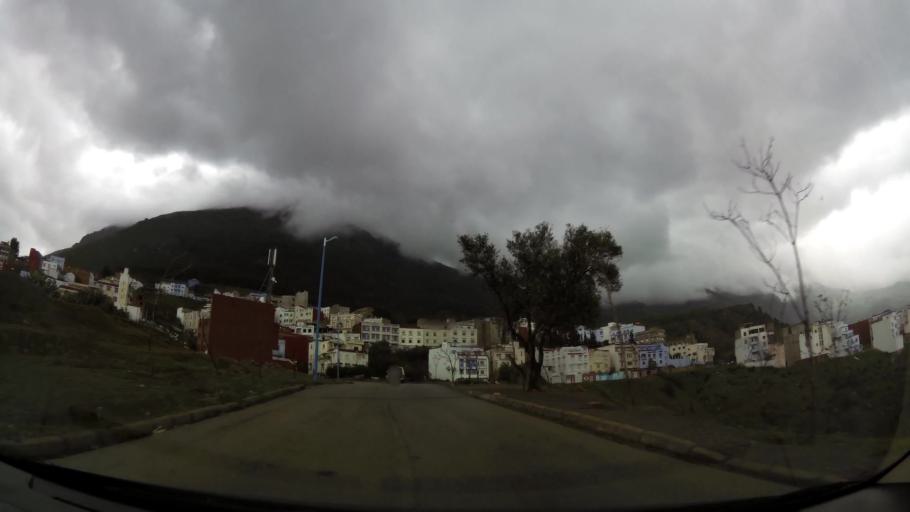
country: MA
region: Tanger-Tetouan
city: Chefchaouene
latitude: 35.1750
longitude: -5.2729
